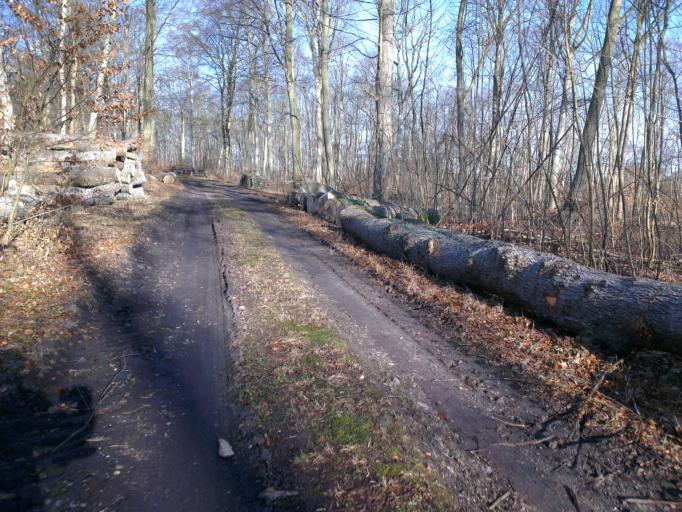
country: DK
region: Capital Region
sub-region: Halsnaes Kommune
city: Frederiksvaerk
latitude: 55.9104
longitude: 12.0070
